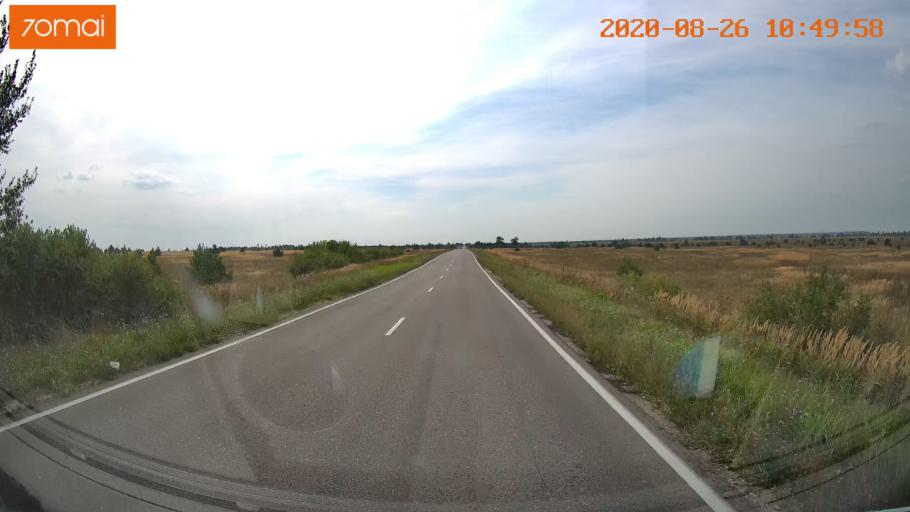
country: RU
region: Rjazan
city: Lashma
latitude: 54.6939
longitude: 41.1575
